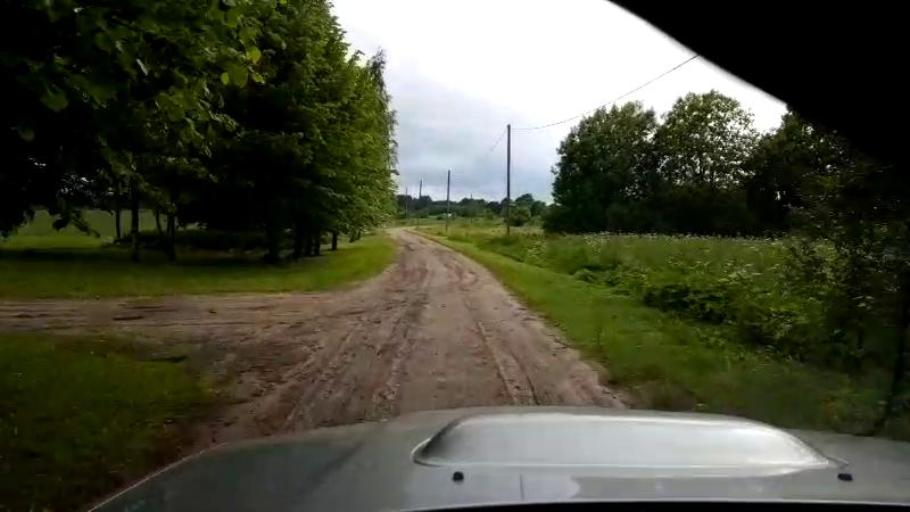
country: EE
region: Paernumaa
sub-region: Halinga vald
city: Parnu-Jaagupi
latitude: 58.5624
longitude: 24.5781
